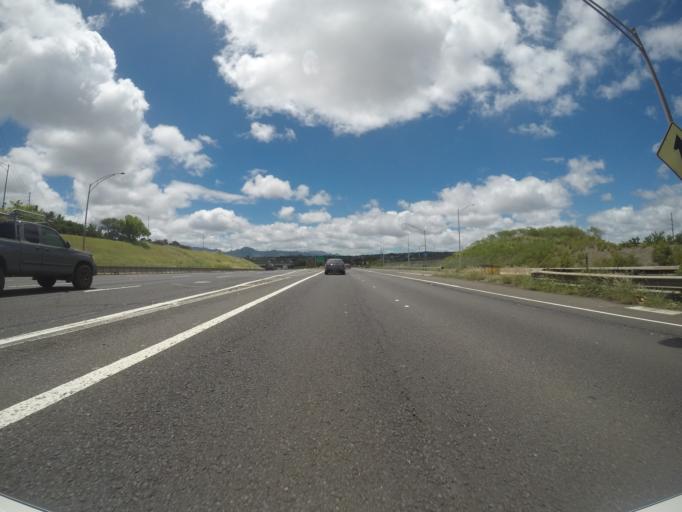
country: US
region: Hawaii
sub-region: Honolulu County
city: Pearl City, Manana
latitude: 21.3965
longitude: -157.9849
